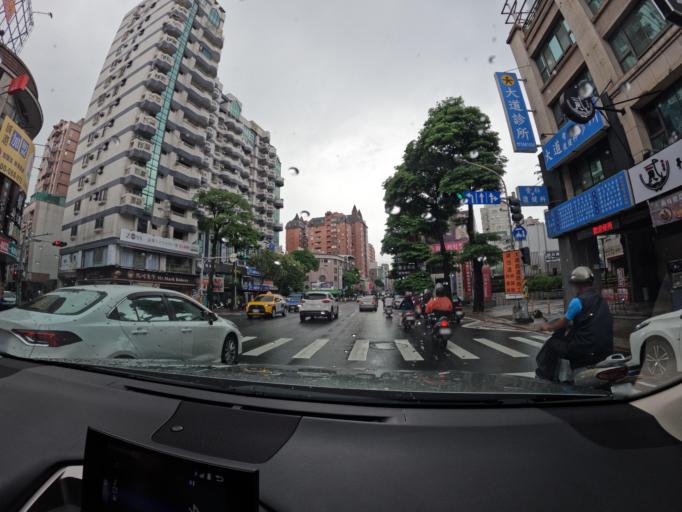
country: TW
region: Kaohsiung
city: Kaohsiung
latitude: 22.6618
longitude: 120.3086
